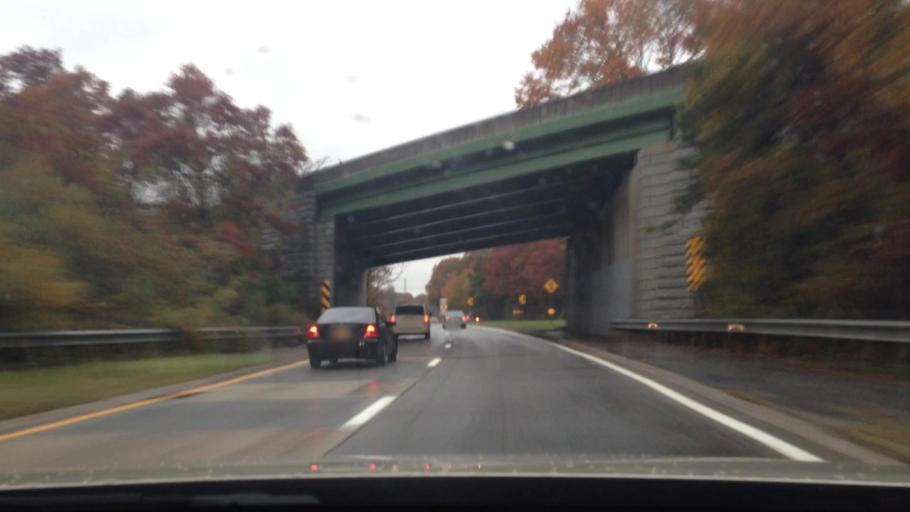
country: US
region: New York
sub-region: Suffolk County
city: Bay Wood
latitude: 40.7467
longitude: -73.2789
